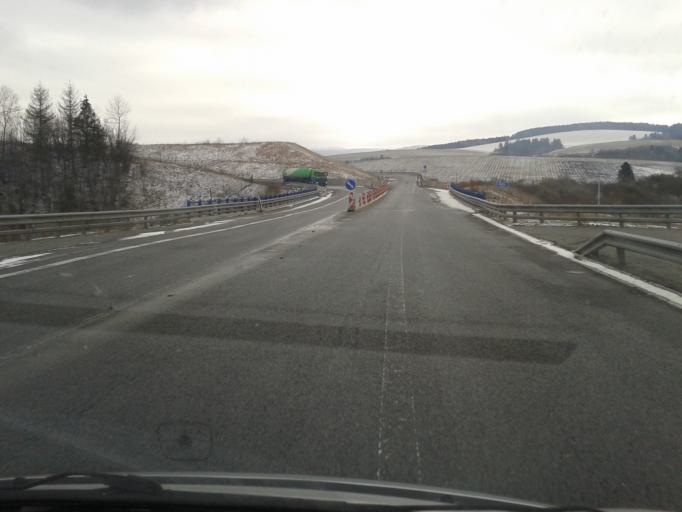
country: SK
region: Zilinsky
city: Tvrdosin
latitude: 49.3454
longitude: 19.5755
